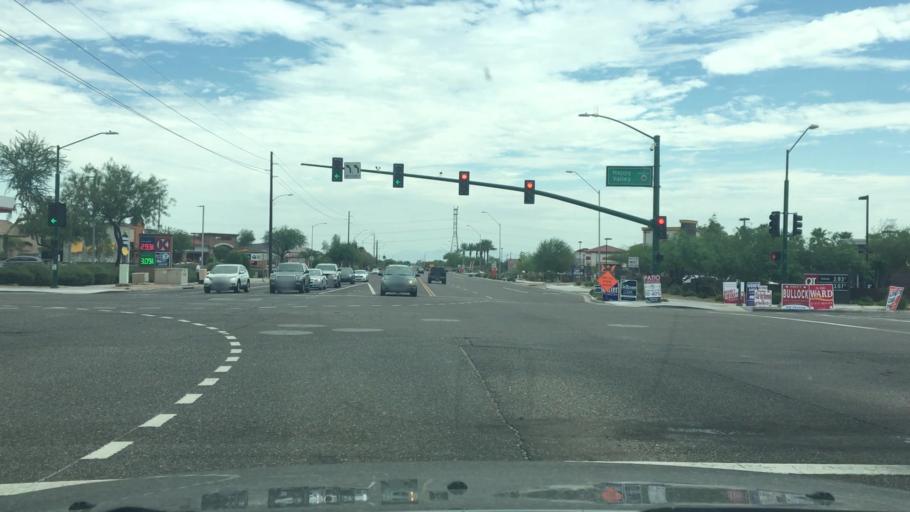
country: US
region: Arizona
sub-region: Maricopa County
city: Sun City
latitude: 33.7124
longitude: -112.2031
